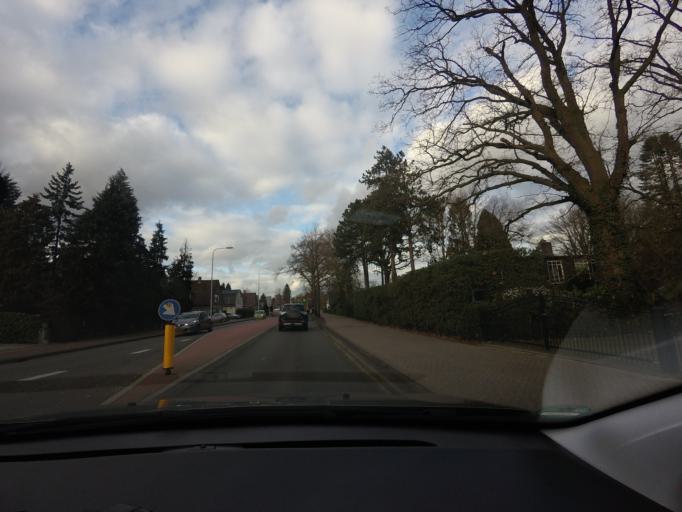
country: NL
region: Gelderland
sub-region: Gemeente Lochem
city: Gorssel
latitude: 52.2040
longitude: 6.1959
